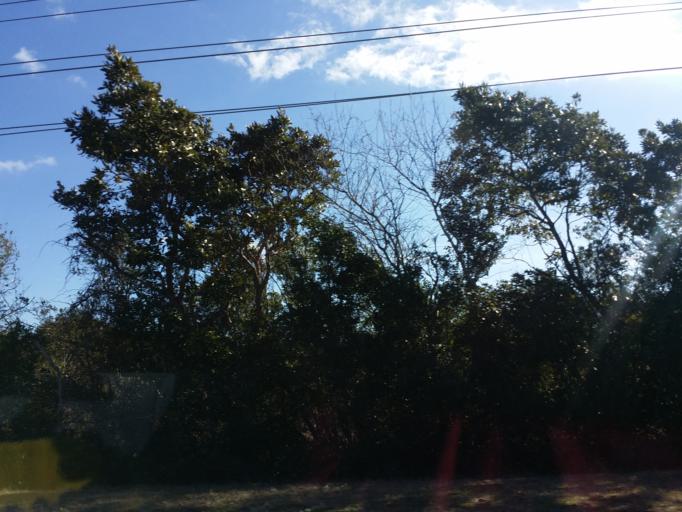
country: US
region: North Carolina
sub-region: Onslow County
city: Sneads Ferry
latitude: 34.4909
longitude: -77.4269
